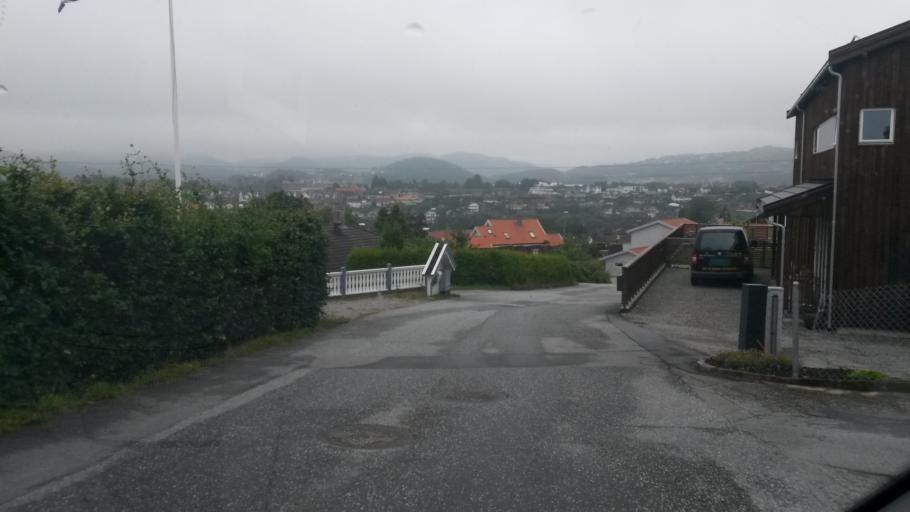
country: NO
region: Rogaland
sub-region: Sandnes
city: Sandnes
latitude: 58.8315
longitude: 5.7127
